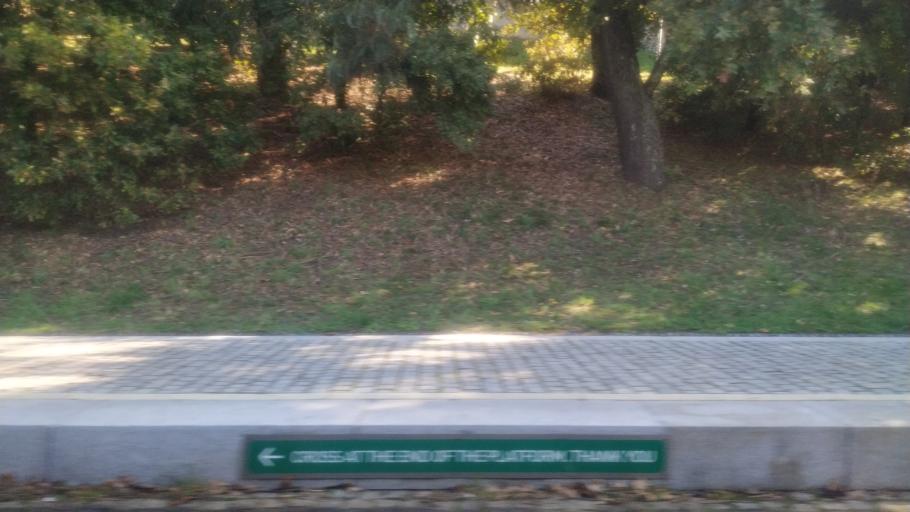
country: PT
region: Porto
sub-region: Matosinhos
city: Senhora da Hora
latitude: 41.1804
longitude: -8.6661
